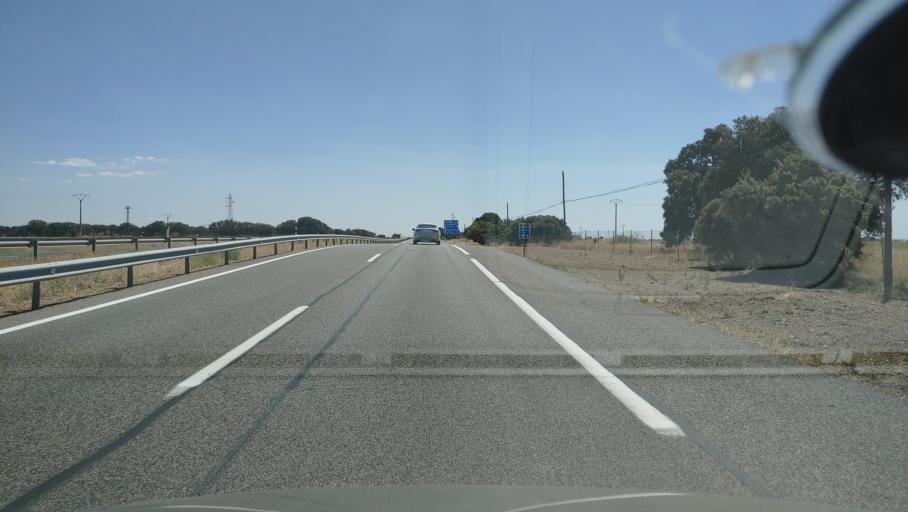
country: ES
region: Castille-La Mancha
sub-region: Provincia de Ciudad Real
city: Villarta de San Juan
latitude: 39.1927
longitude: -3.4028
